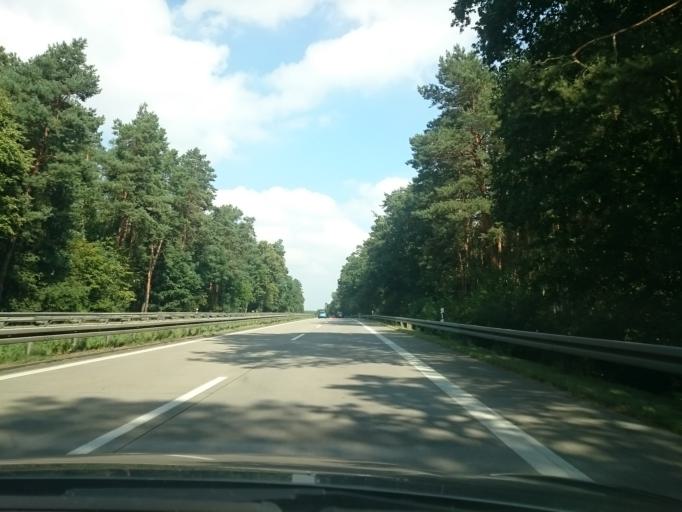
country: DE
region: Brandenburg
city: Althuttendorf
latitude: 52.9275
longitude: 13.7805
